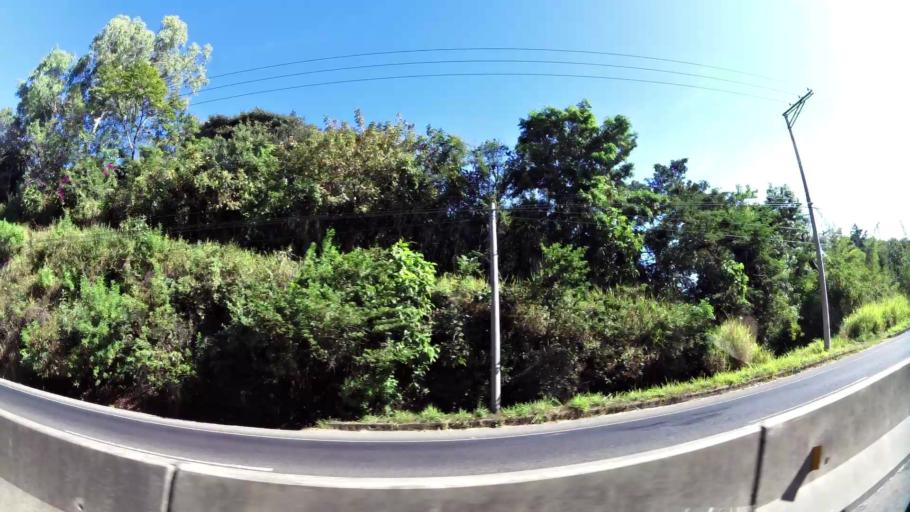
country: SV
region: Santa Ana
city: Santa Ana
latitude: 13.9454
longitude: -89.5555
